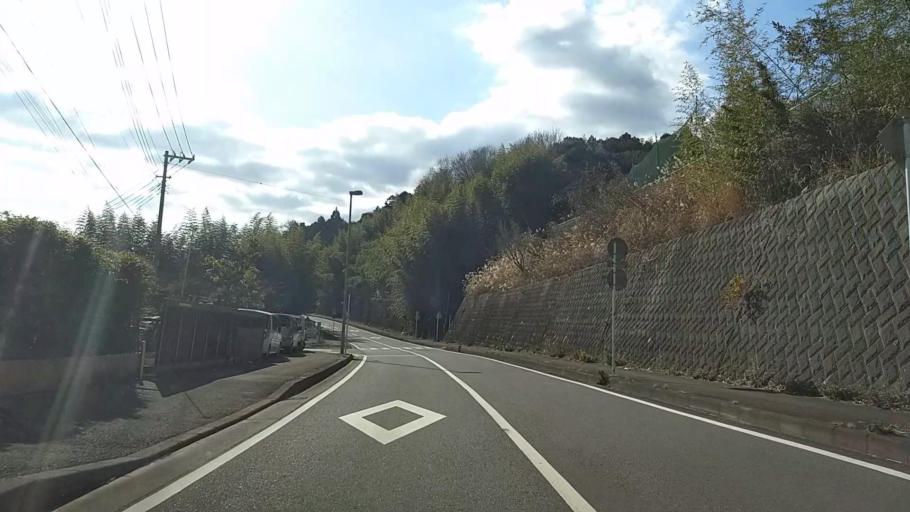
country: JP
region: Kanagawa
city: Isehara
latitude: 35.4573
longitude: 139.2914
